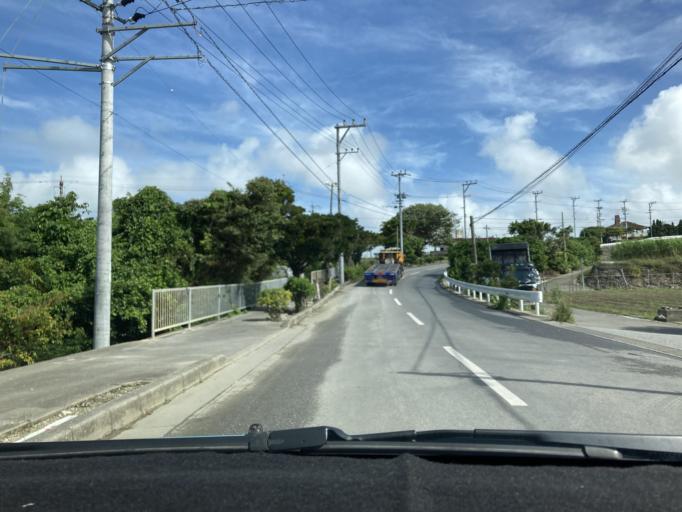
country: JP
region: Okinawa
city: Itoman
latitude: 26.1048
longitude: 127.6628
